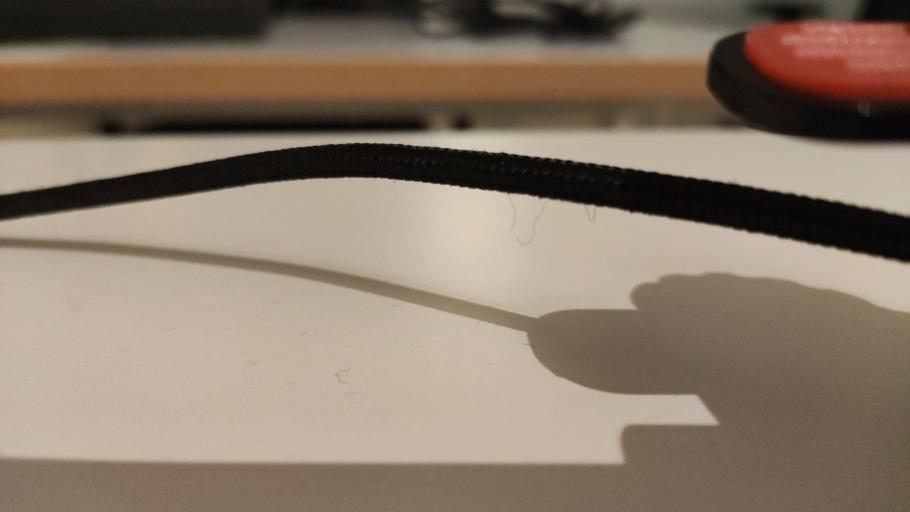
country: RU
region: Moskovskaya
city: Malaya Dubna
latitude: 55.8571
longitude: 38.9623
